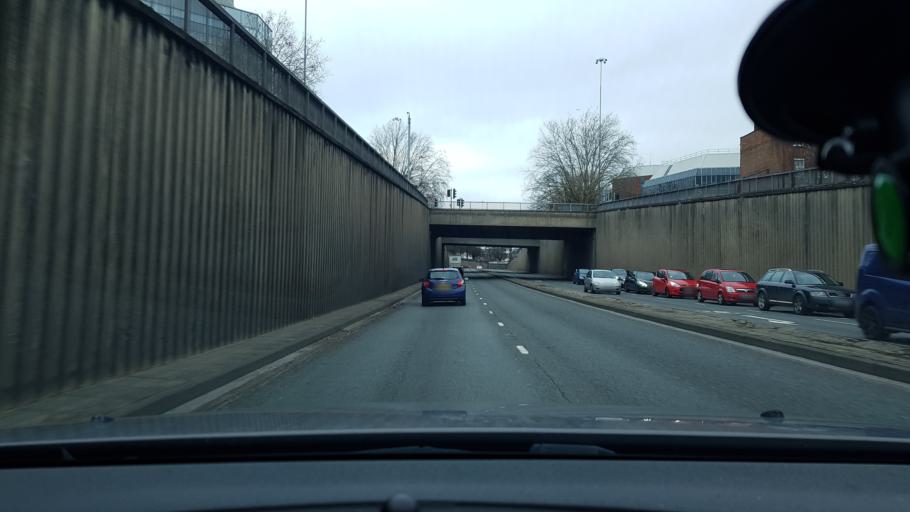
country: GB
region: England
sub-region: Reading
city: Reading
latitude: 51.4513
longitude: -0.9769
